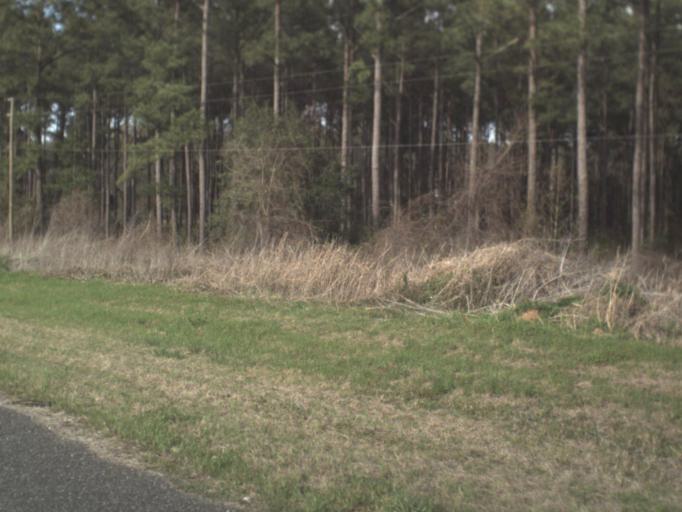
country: US
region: Florida
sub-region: Jefferson County
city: Monticello
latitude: 30.6395
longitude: -83.8739
